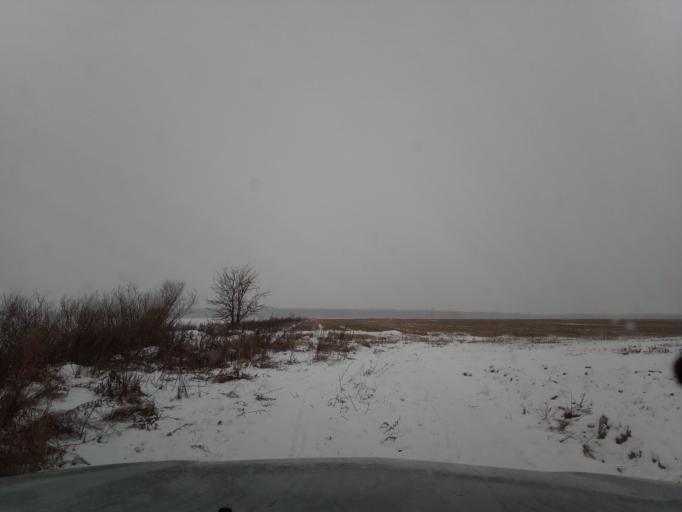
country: LT
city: Ramygala
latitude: 55.4838
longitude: 24.2931
